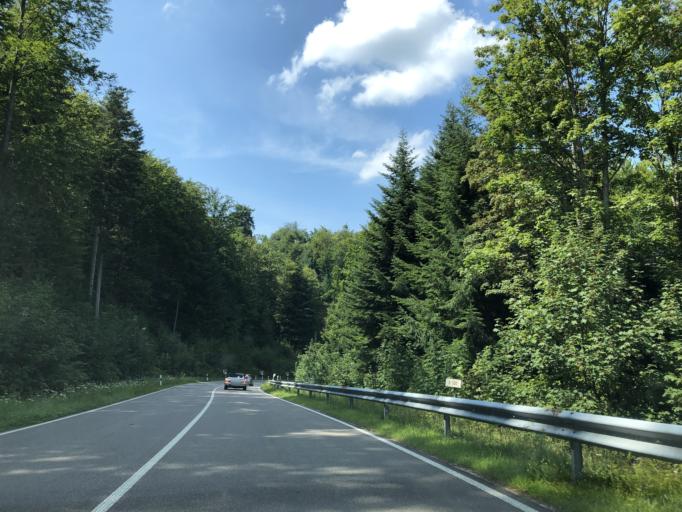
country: DE
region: Baden-Wuerttemberg
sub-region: Karlsruhe Region
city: Baden-Baden
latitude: 48.7127
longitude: 8.2376
